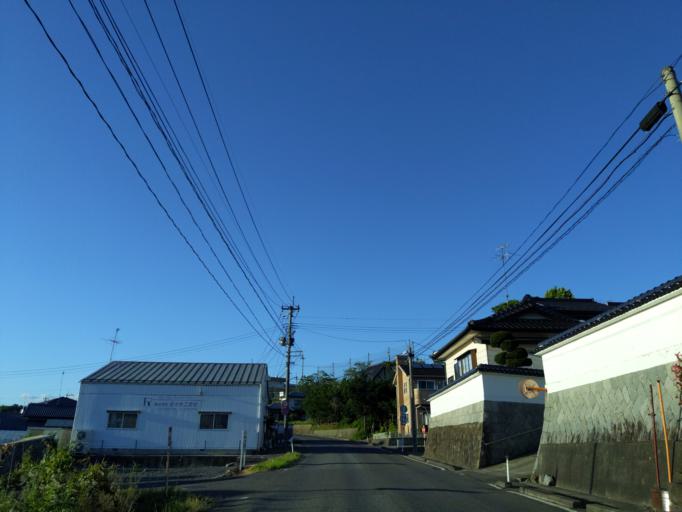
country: JP
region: Fukushima
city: Koriyama
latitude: 37.4013
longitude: 140.4123
